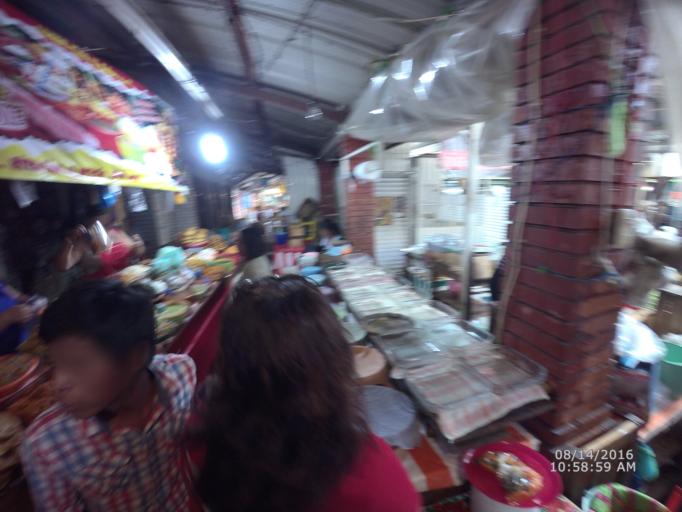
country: MX
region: Oaxaca
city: Oaxaca de Juarez
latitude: 17.0587
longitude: -96.7340
